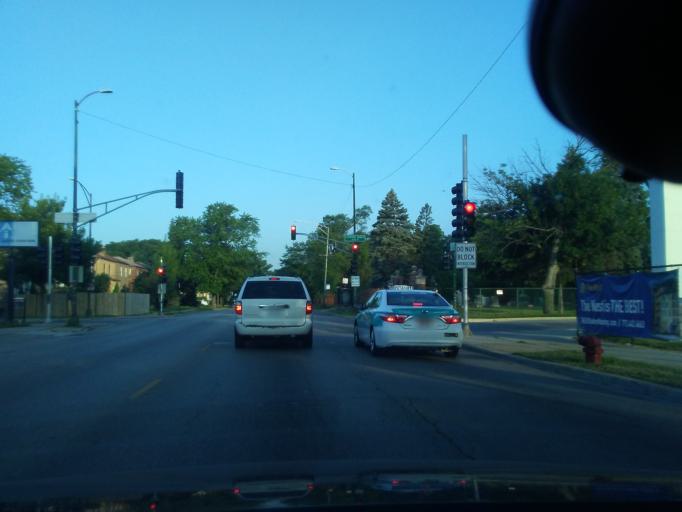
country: US
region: Illinois
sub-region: Cook County
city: Lincolnwood
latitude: 41.9757
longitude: -87.7180
